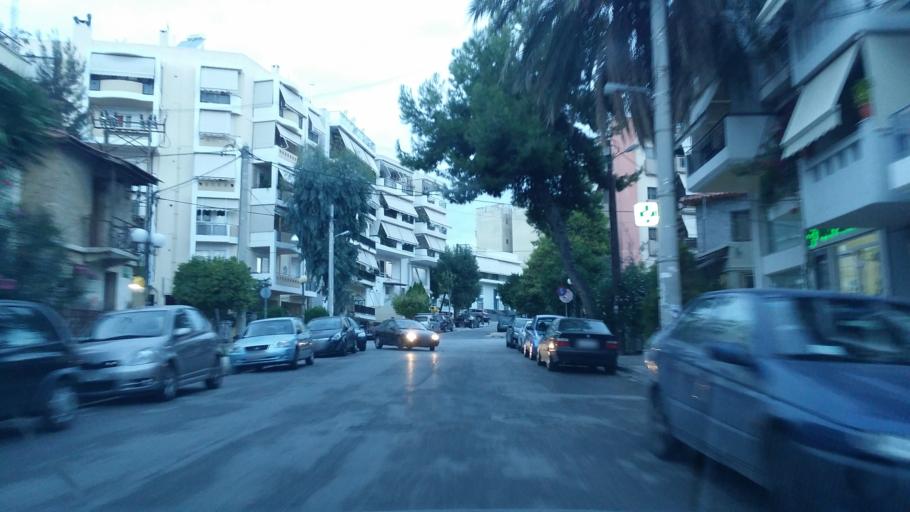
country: GR
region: Attica
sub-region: Nomarchia Athinas
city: Nea Ionia
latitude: 38.0442
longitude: 23.7508
